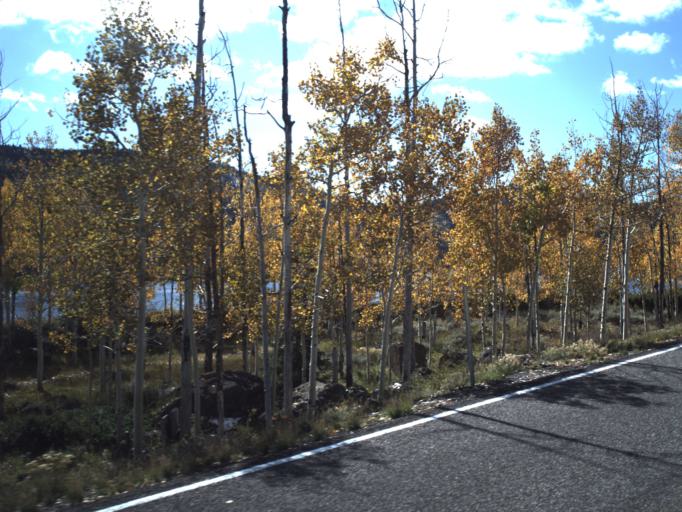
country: US
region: Utah
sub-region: Wayne County
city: Loa
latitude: 38.5545
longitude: -111.7158
